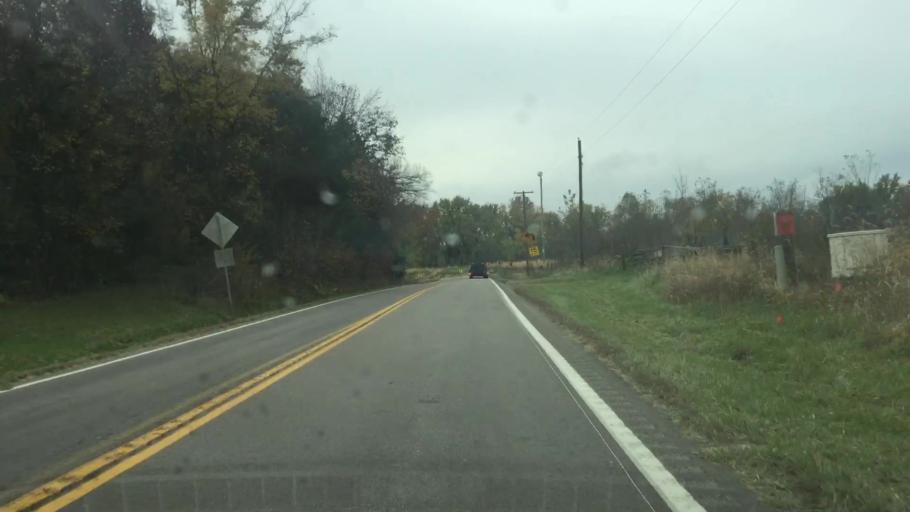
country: US
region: Missouri
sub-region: Gasconade County
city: Hermann
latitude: 38.7069
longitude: -91.6244
